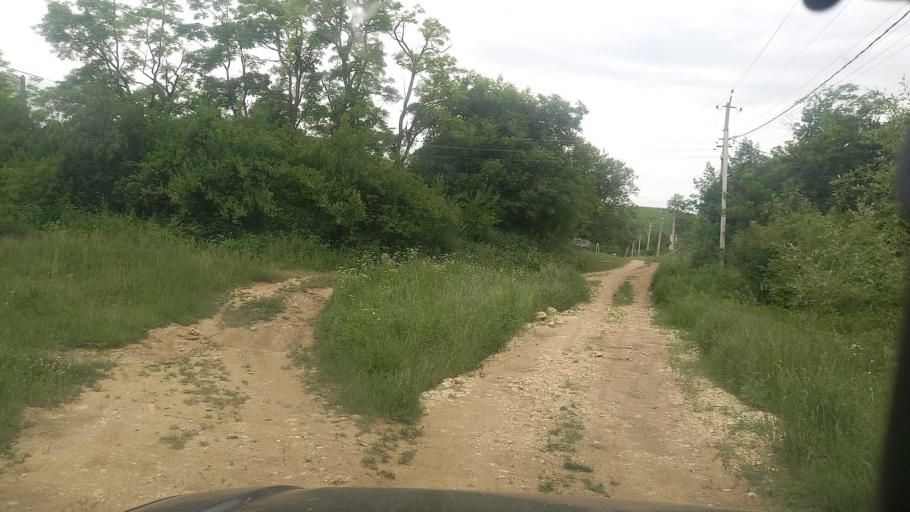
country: RU
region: Krasnodarskiy
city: Peredovaya
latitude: 44.0840
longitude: 41.3698
